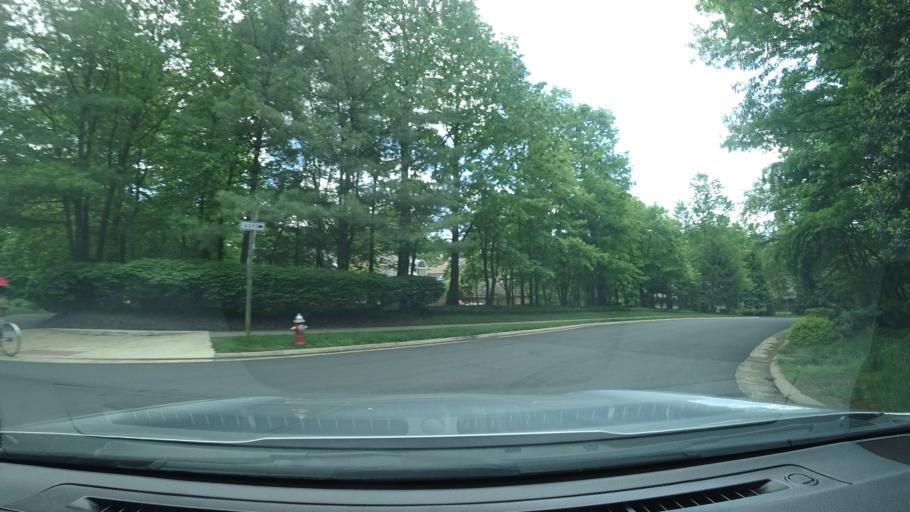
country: US
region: Virginia
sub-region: Fairfax County
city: Reston
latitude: 38.9711
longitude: -77.3458
